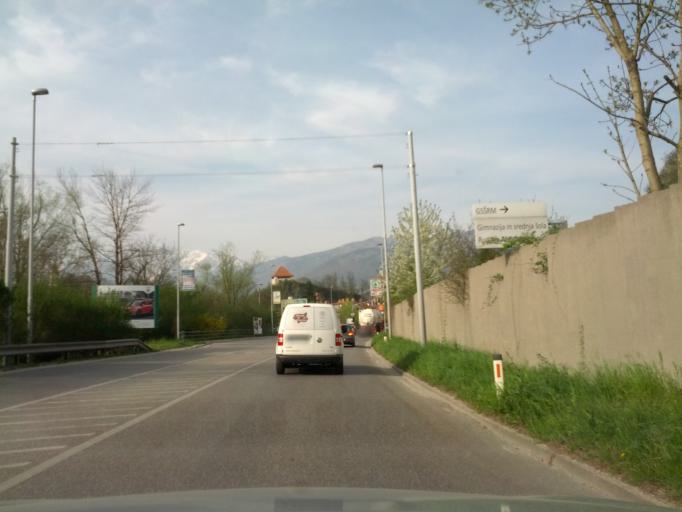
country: SI
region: Kamnik
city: Kamnik
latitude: 46.2202
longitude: 14.6103
